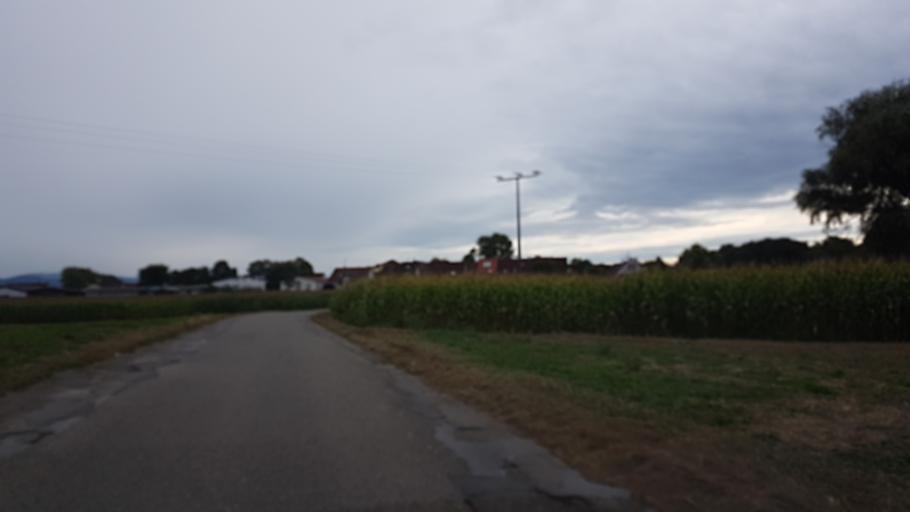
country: DE
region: Baden-Wuerttemberg
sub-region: Freiburg Region
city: Merdingen
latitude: 47.9938
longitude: 7.7185
